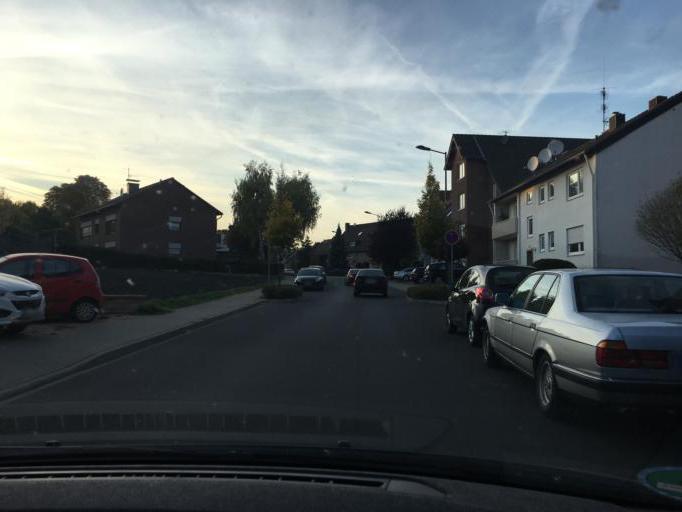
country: DE
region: North Rhine-Westphalia
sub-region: Regierungsbezirk Koln
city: Hurth
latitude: 50.8660
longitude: 6.8848
